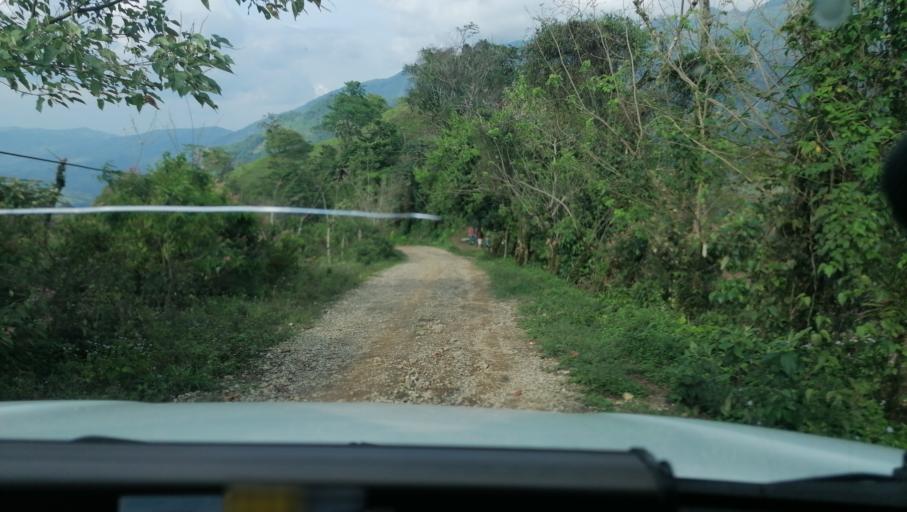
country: MX
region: Chiapas
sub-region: Tapilula
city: San Francisco Jacona
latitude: 17.3160
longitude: -93.0992
